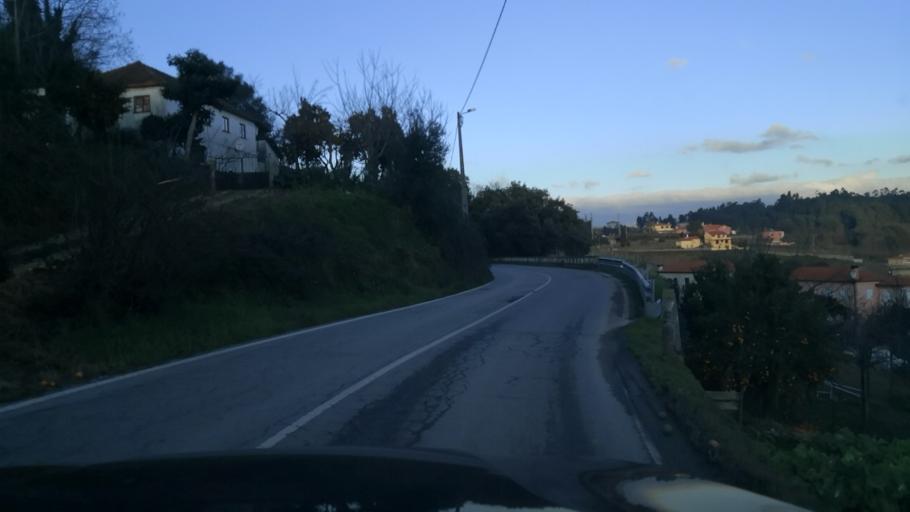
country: PT
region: Vila Real
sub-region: Mondim de Basto
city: Mondim de Basto
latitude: 41.4457
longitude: -7.9647
